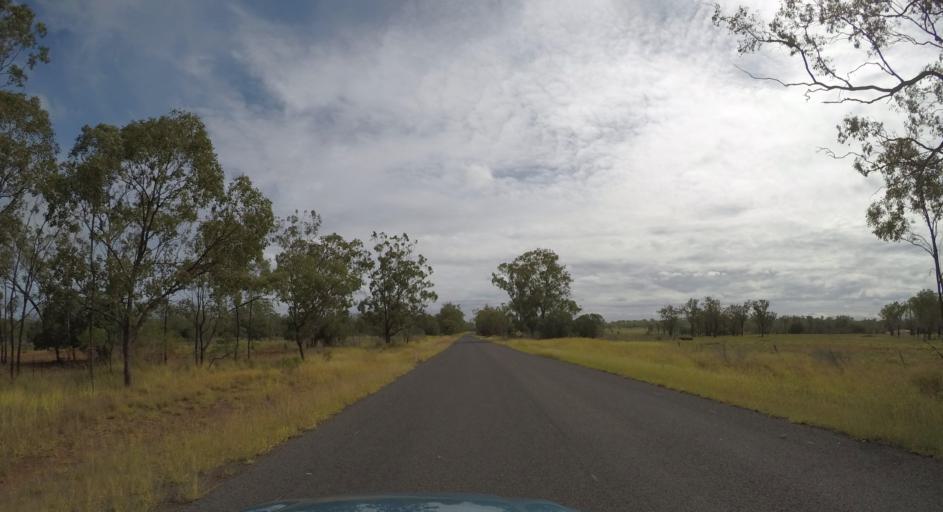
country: AU
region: Queensland
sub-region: Western Downs
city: Dalby
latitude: -27.0526
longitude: 151.3159
